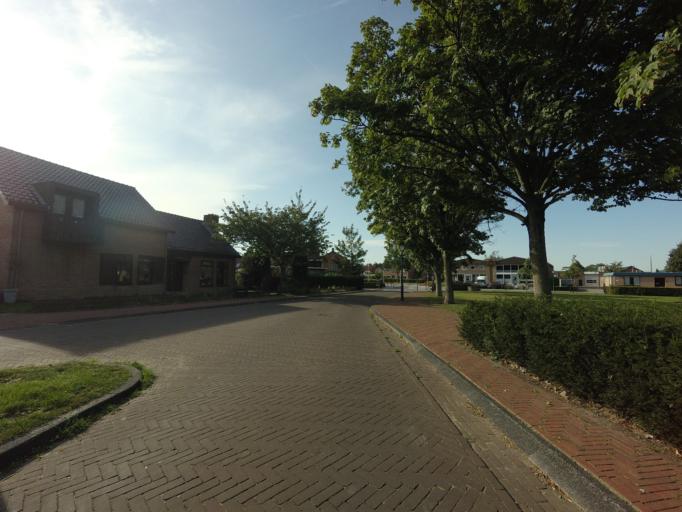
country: NL
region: Utrecht
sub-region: Gemeente Lopik
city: Lopik
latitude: 51.9550
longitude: 4.9633
